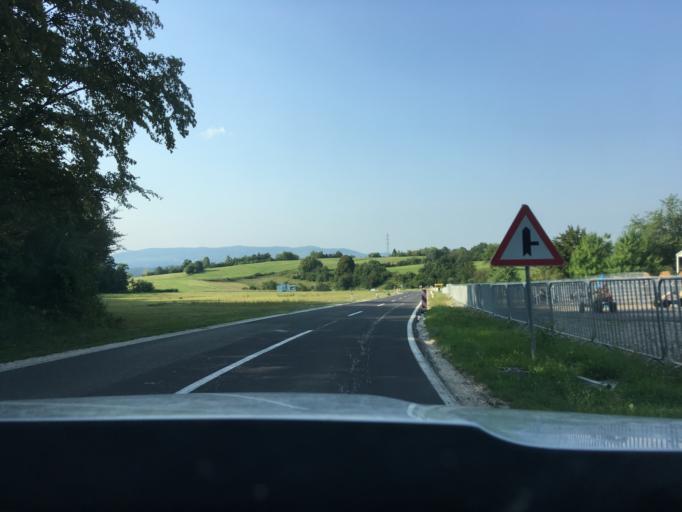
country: SI
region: Novo Mesto
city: Novo Mesto
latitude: 45.7595
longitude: 15.2001
